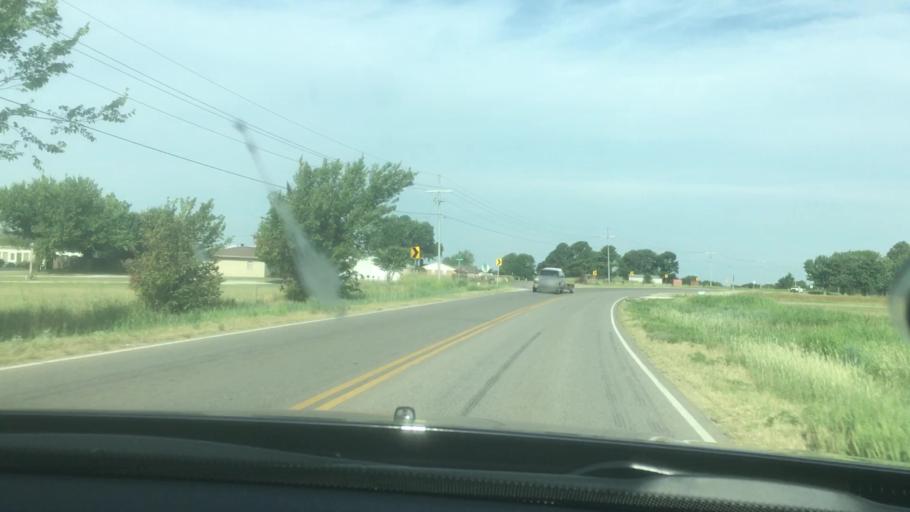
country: US
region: Oklahoma
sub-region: Pontotoc County
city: Ada
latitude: 34.7822
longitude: -96.7825
